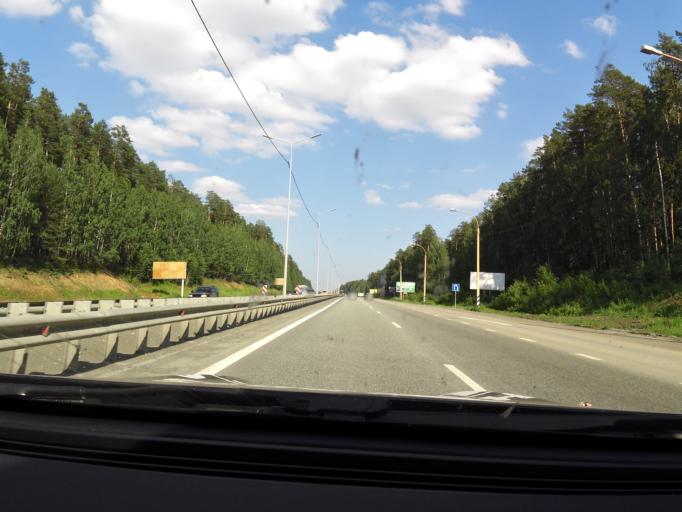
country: RU
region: Sverdlovsk
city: Shirokaya Rechka
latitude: 56.8258
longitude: 60.4492
